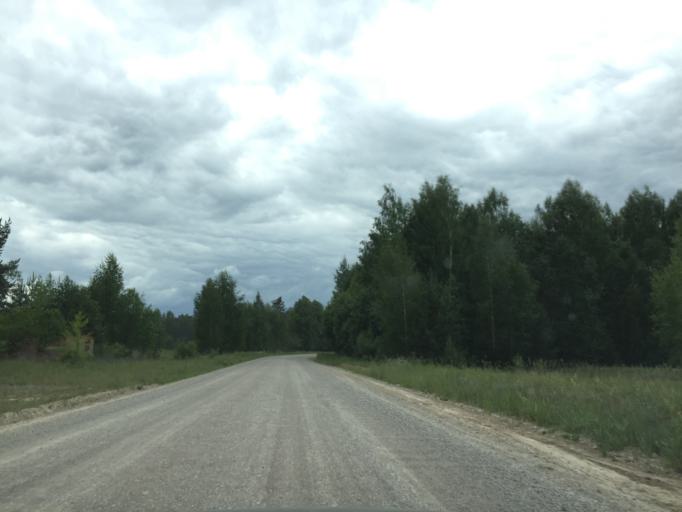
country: LV
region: Vilanu
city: Vilani
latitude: 56.4424
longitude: 27.0682
